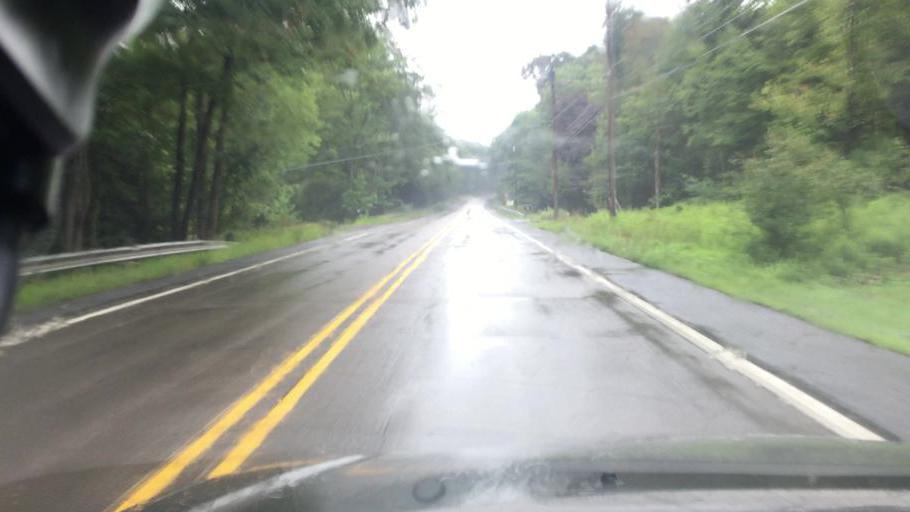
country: US
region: Pennsylvania
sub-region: Luzerne County
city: Freeland
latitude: 41.0408
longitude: -75.8368
